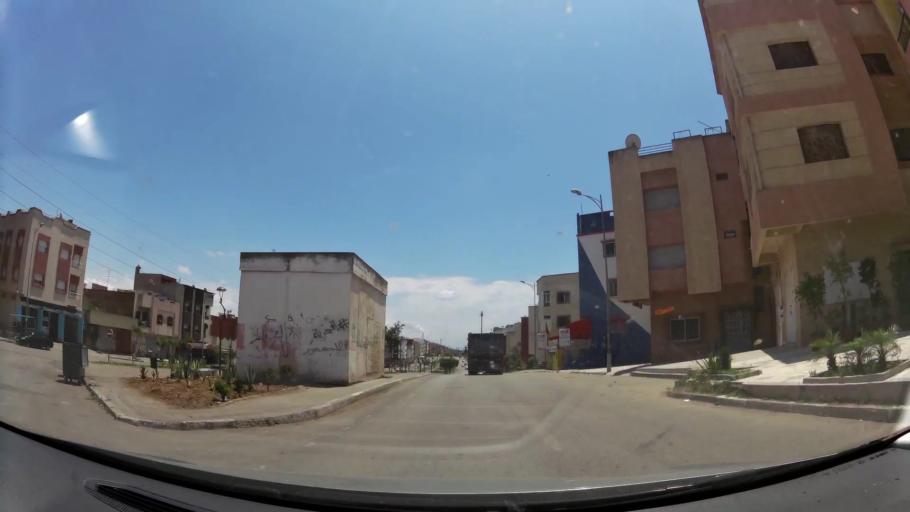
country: MA
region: Gharb-Chrarda-Beni Hssen
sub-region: Kenitra Province
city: Kenitra
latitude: 34.2594
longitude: -6.6163
